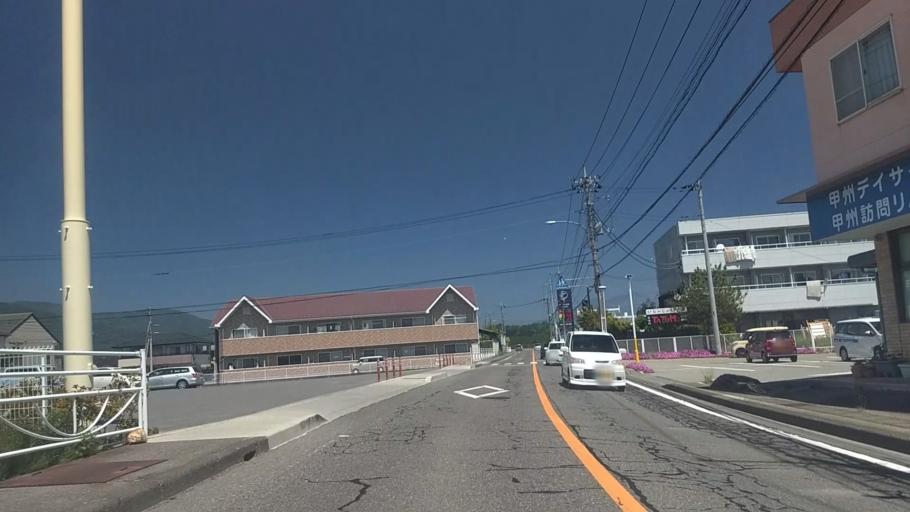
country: JP
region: Yamanashi
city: Nirasaki
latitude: 35.6955
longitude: 138.4567
